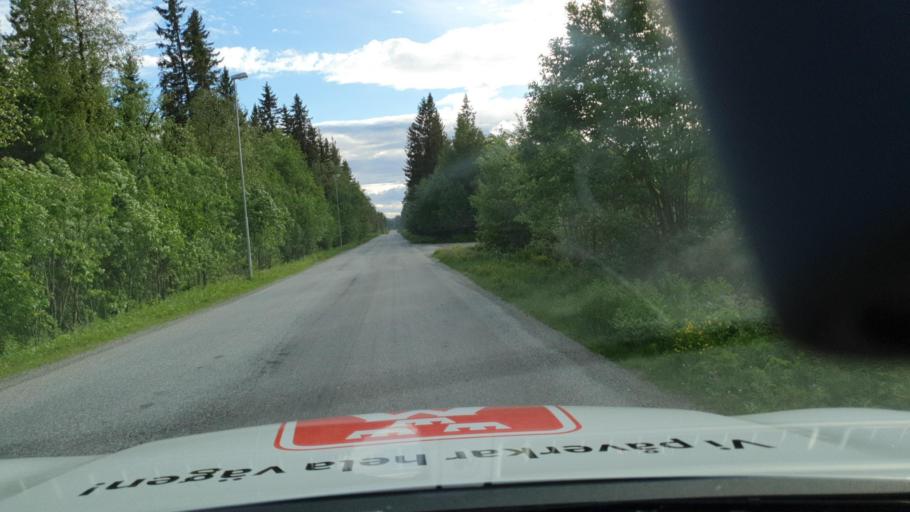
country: SE
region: Vaesterbotten
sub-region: Storumans Kommun
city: Storuman
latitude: 65.0714
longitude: 17.1310
